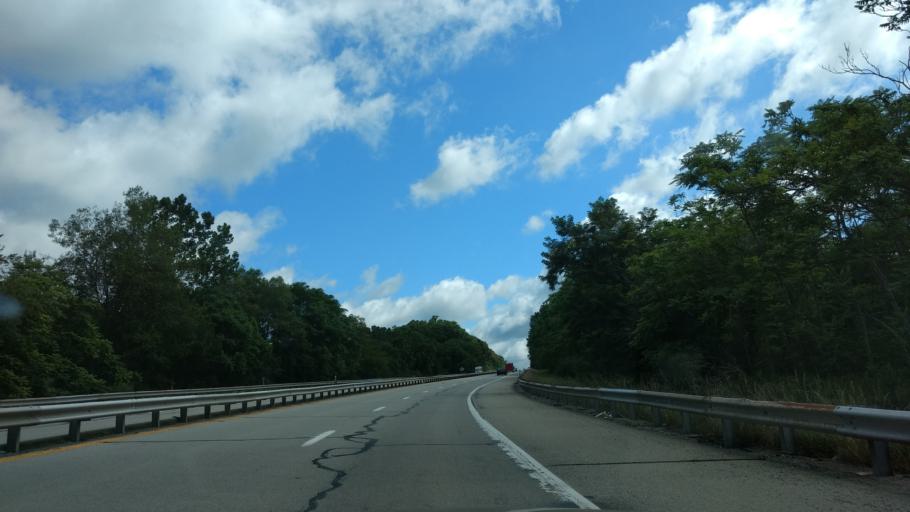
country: US
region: Pennsylvania
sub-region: Armstrong County
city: Apollo
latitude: 40.5170
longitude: -79.6434
